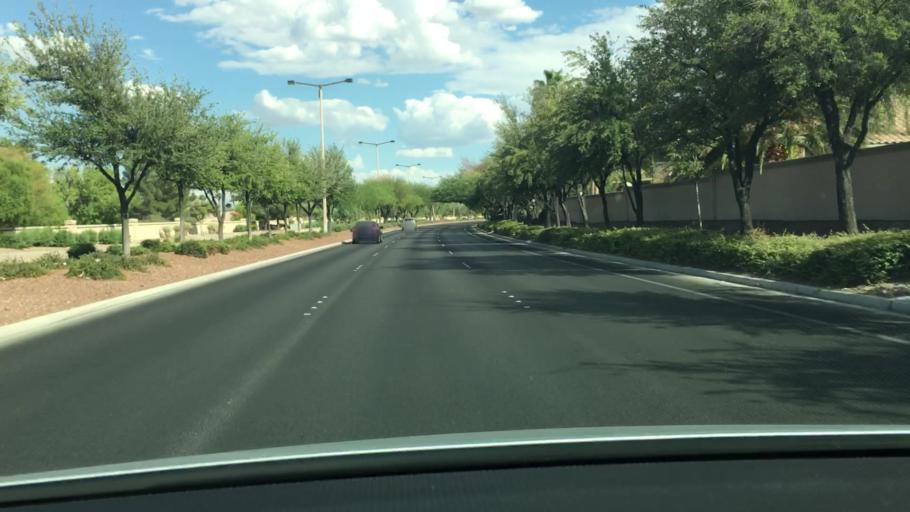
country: US
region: Nevada
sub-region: Clark County
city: Summerlin South
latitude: 36.2045
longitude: -115.2909
